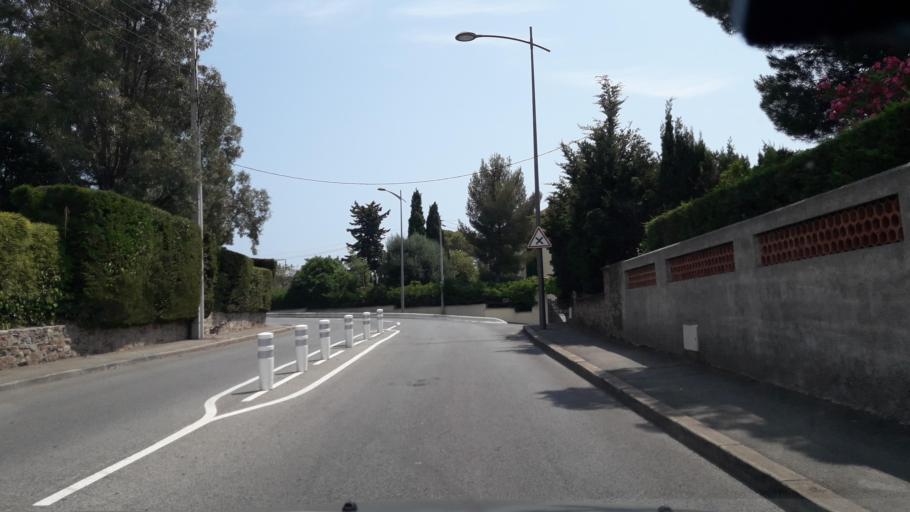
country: FR
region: Provence-Alpes-Cote d'Azur
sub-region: Departement du Var
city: Saint-Raphael
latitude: 43.4207
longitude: 6.7842
